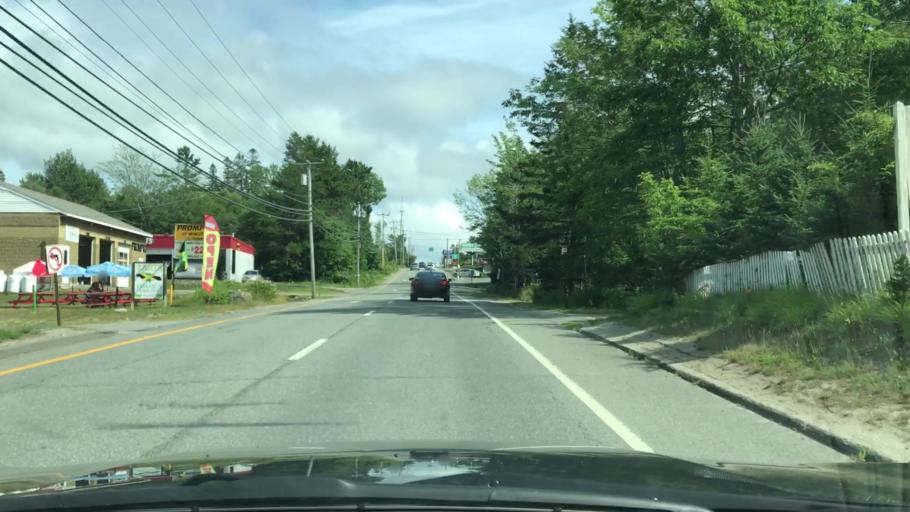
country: US
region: Maine
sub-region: Hancock County
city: Ellsworth
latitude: 44.5282
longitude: -68.4030
